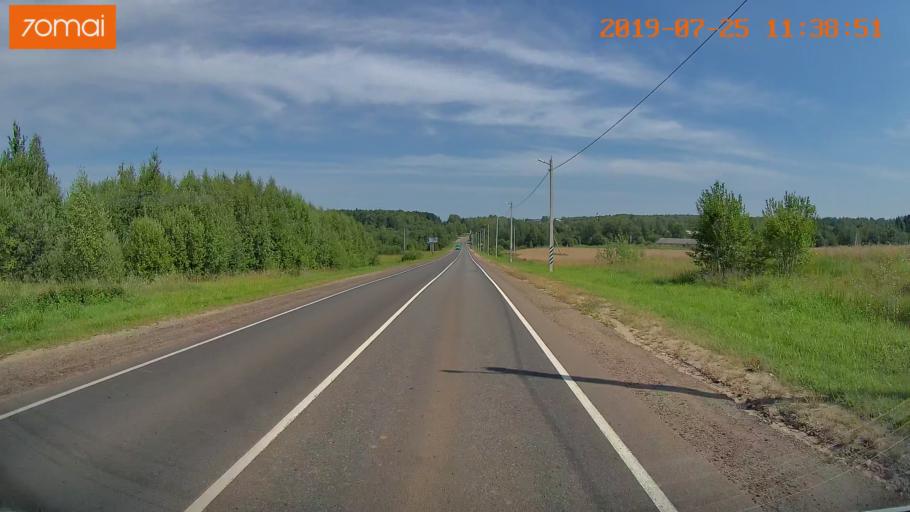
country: RU
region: Ivanovo
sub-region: Privolzhskiy Rayon
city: Ples
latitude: 57.4447
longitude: 41.4892
